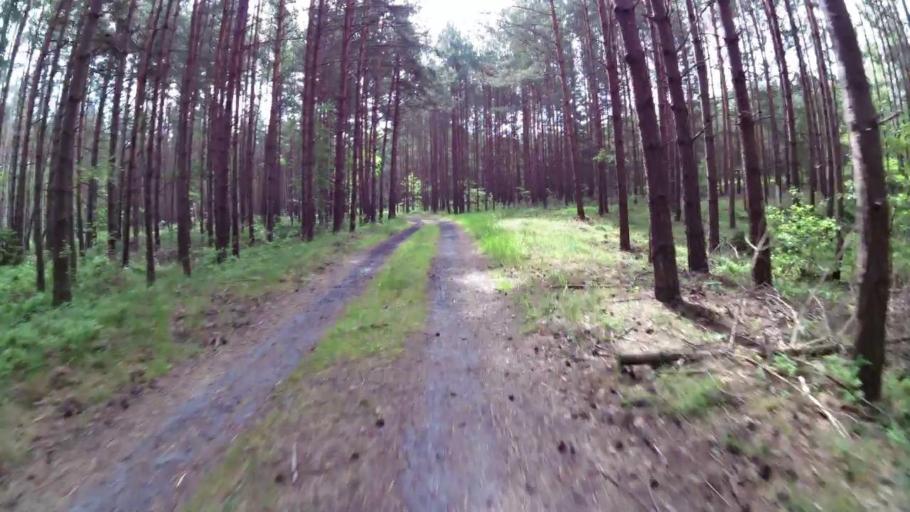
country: PL
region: West Pomeranian Voivodeship
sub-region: Swinoujscie
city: Swinoujscie
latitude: 53.9072
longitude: 14.3212
